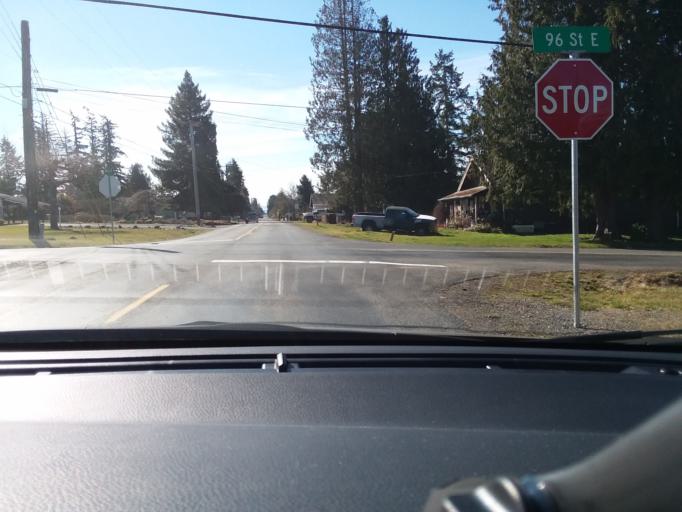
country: US
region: Washington
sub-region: Pierce County
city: Summit
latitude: 47.1701
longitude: -122.3784
